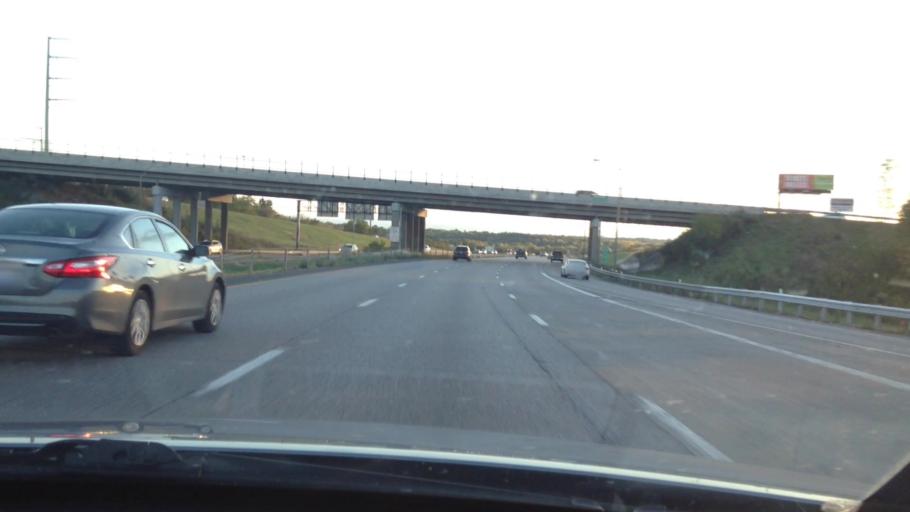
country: US
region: Missouri
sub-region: Jackson County
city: Raytown
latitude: 39.0567
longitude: -94.4929
